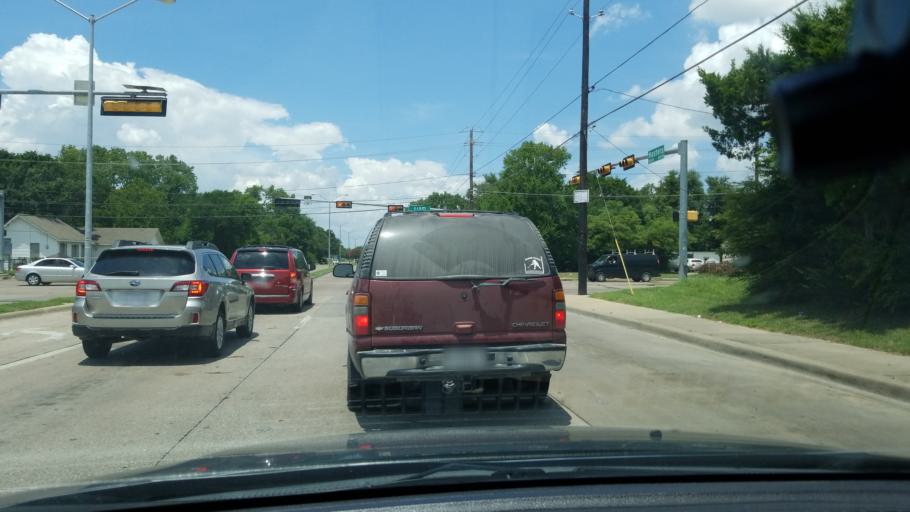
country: US
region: Texas
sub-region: Dallas County
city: Balch Springs
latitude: 32.7191
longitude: -96.6484
